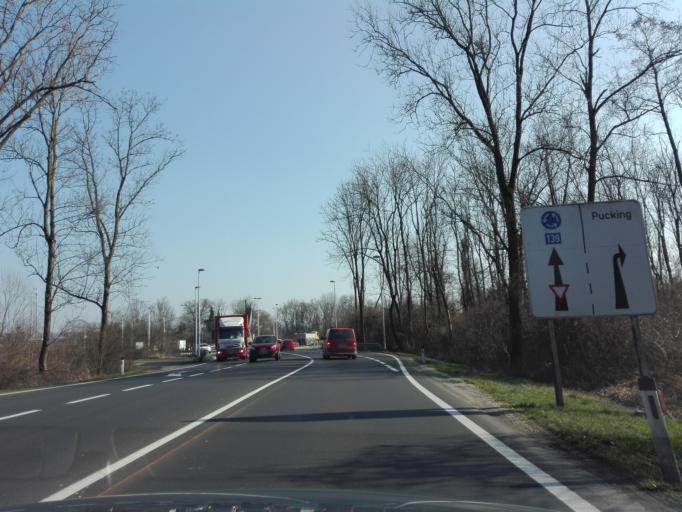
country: AT
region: Upper Austria
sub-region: Politischer Bezirk Linz-Land
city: Traun
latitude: 48.2102
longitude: 14.2406
